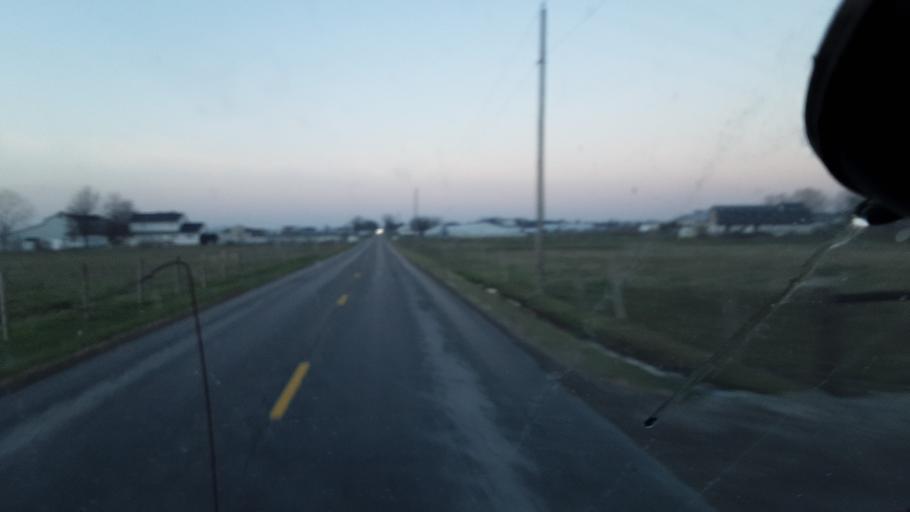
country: US
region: Indiana
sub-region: Allen County
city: Grabill
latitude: 41.2284
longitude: -84.9424
